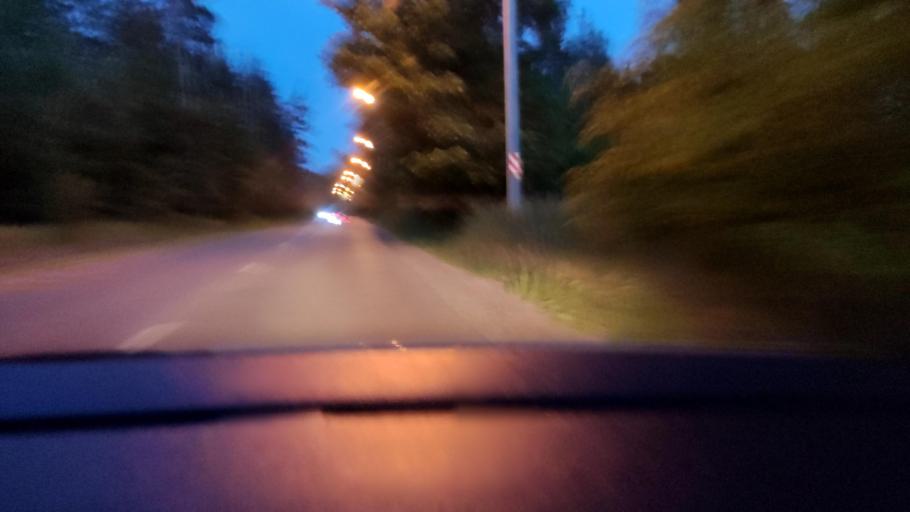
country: RU
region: Voronezj
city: Somovo
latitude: 51.7149
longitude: 39.3250
